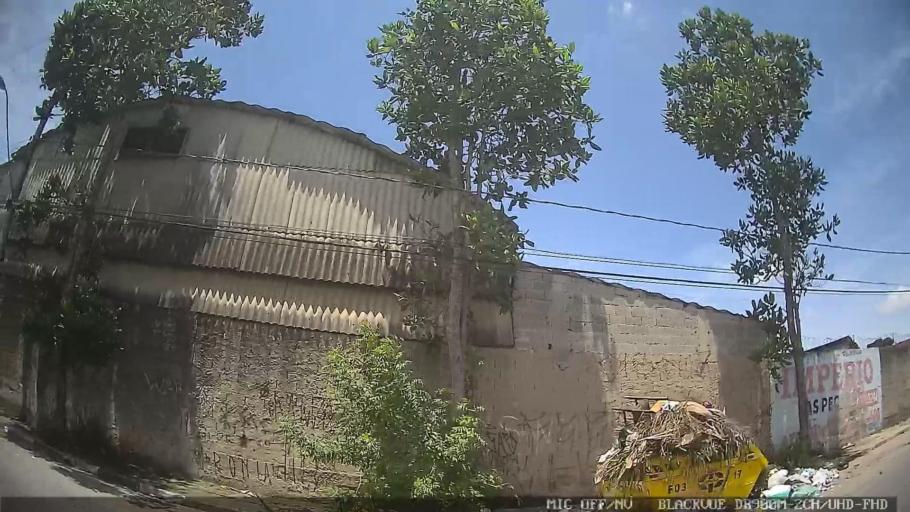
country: BR
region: Sao Paulo
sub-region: Suzano
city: Suzano
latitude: -23.5294
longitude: -46.3163
